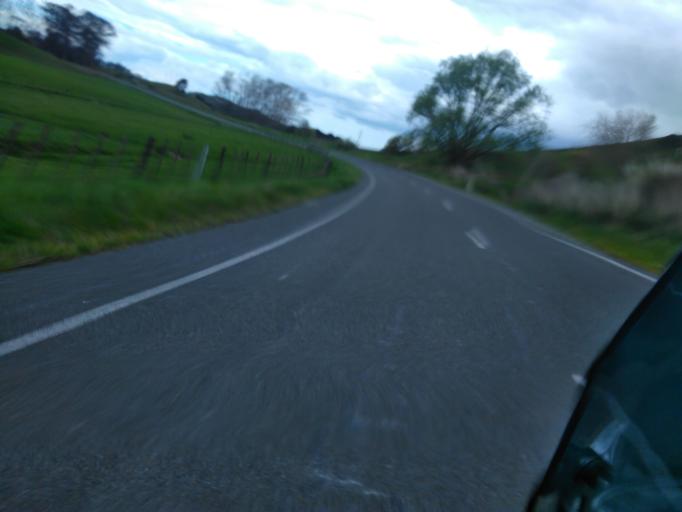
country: NZ
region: Gisborne
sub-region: Gisborne District
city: Gisborne
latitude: -38.6823
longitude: 177.7980
